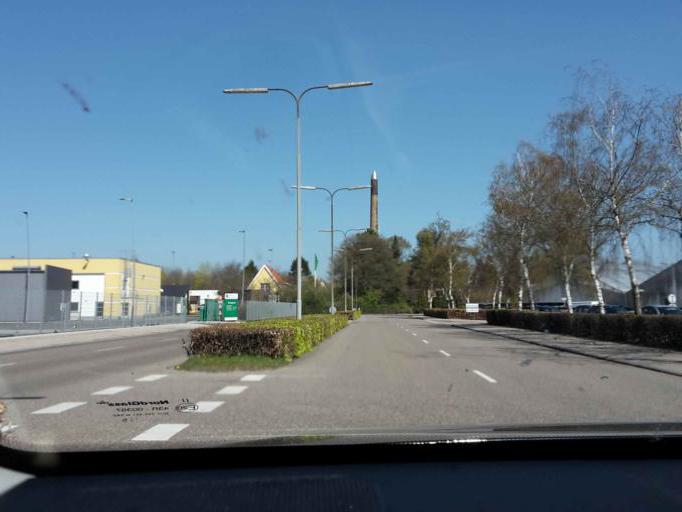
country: DK
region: South Denmark
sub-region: Odense Kommune
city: Odense
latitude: 55.3960
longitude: 10.3553
